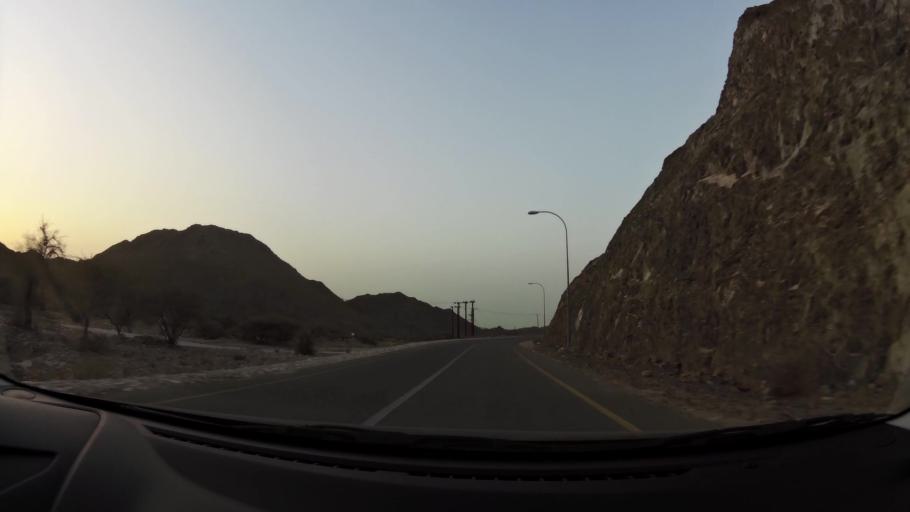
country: OM
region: Muhafazat Masqat
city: Bawshar
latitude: 23.4837
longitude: 58.3295
